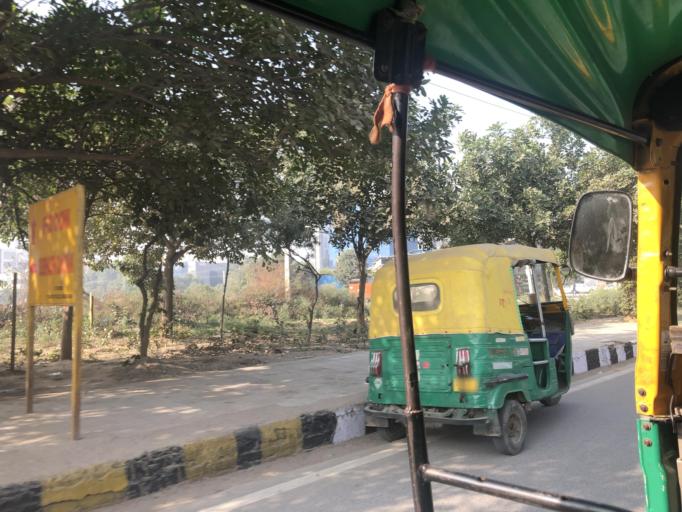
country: IN
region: Haryana
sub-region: Gurgaon
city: Gurgaon
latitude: 28.4527
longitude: 77.0753
